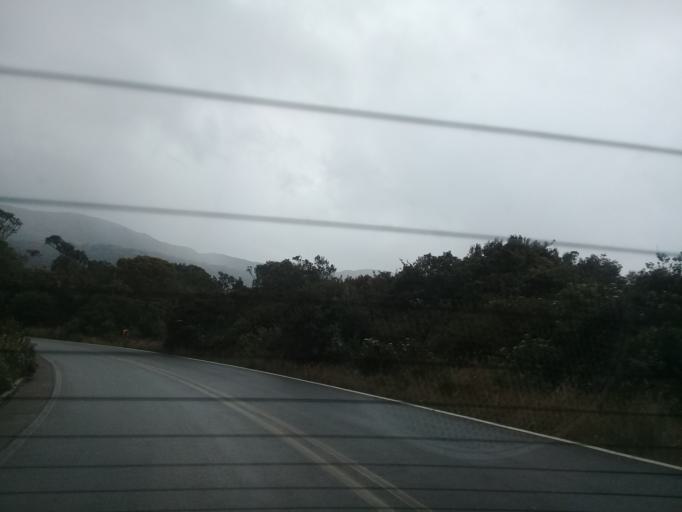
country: CO
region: Cundinamarca
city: Guatavita
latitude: 4.8558
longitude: -73.7533
